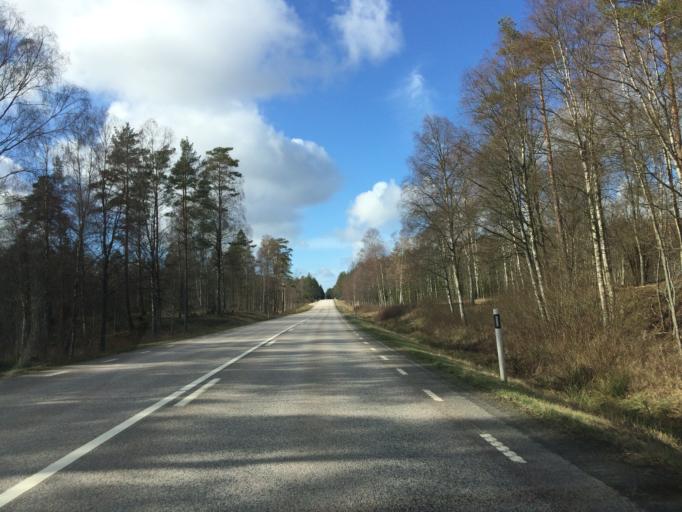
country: SE
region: Halland
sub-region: Laholms Kommun
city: Knared
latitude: 56.4882
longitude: 13.4185
